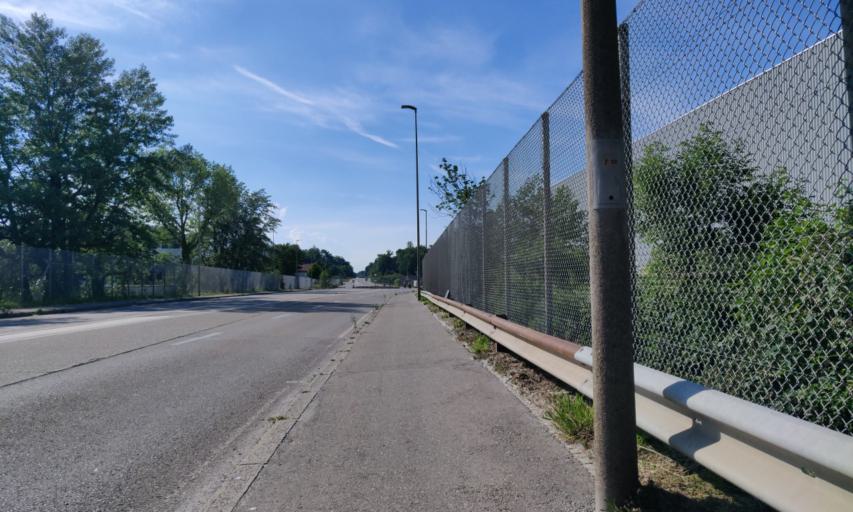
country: CH
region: Basel-Landschaft
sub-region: Bezirk Arlesheim
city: Muttenz
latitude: 47.5360
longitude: 7.6627
